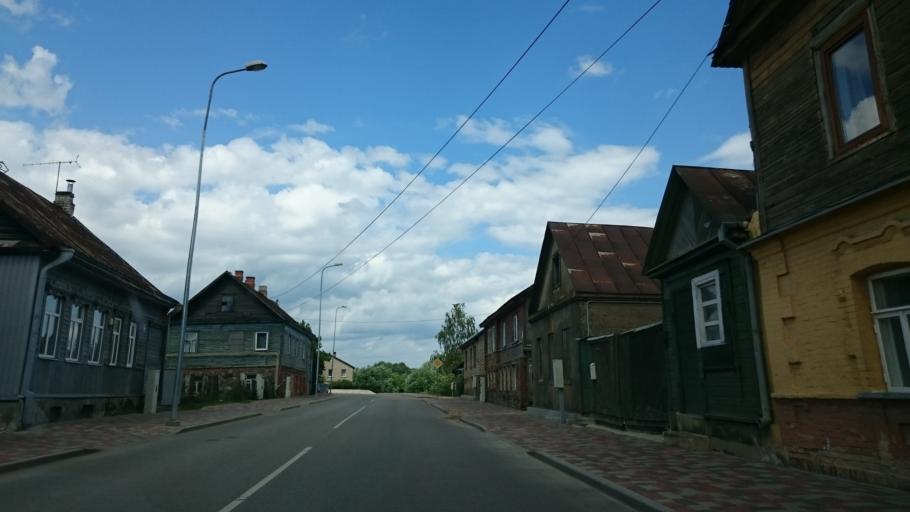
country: LV
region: Ludzas Rajons
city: Ludza
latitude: 56.5495
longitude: 27.7272
